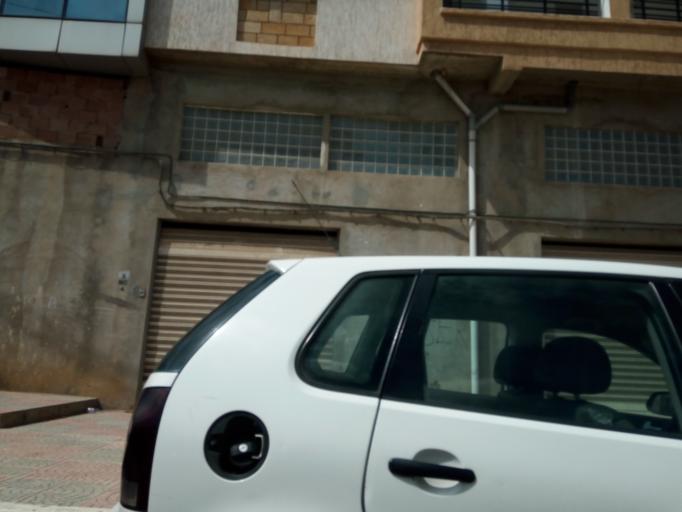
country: DZ
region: Tipaza
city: Douera
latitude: 36.6992
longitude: 2.9747
